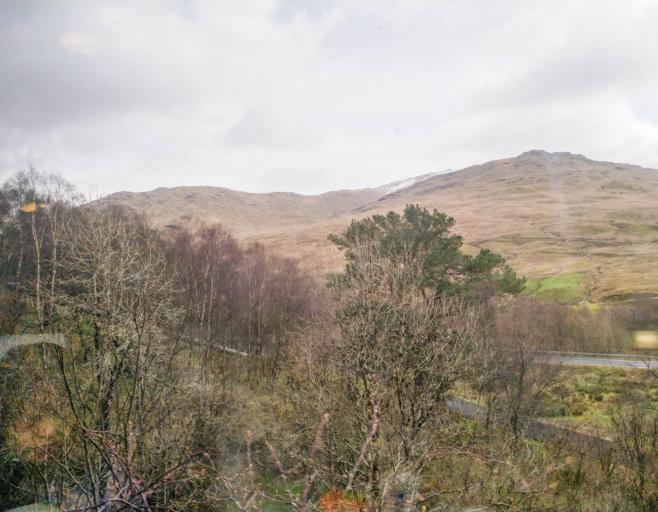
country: GB
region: Scotland
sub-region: Argyll and Bute
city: Garelochhead
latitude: 56.3614
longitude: -4.6749
